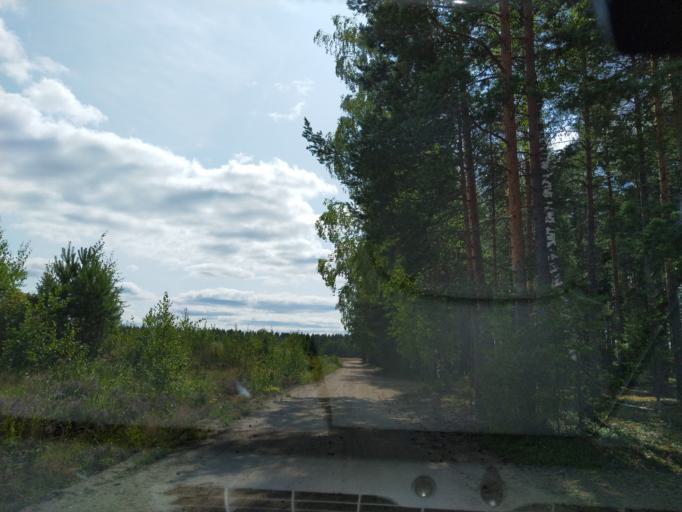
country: FI
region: Uusimaa
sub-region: Helsinki
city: Kaerkoelae
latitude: 60.7454
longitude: 24.1027
